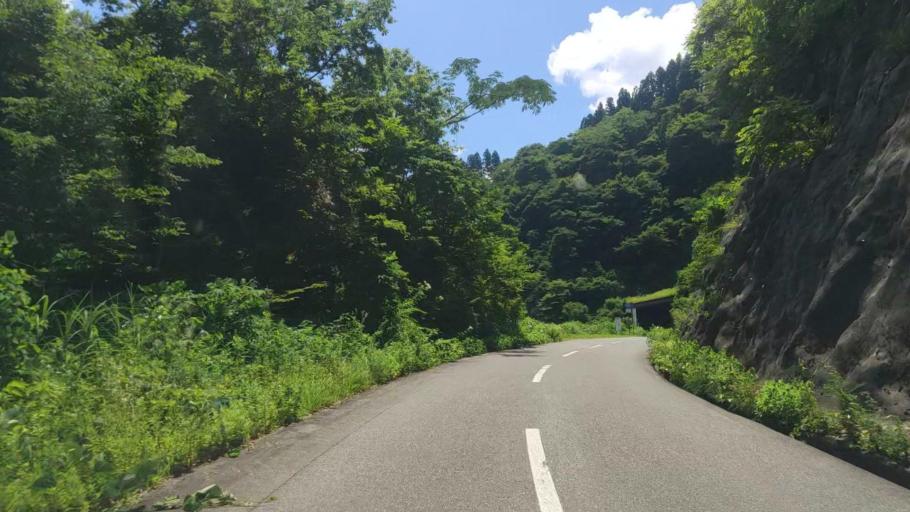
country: JP
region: Fukui
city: Ono
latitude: 35.8964
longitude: 136.5071
